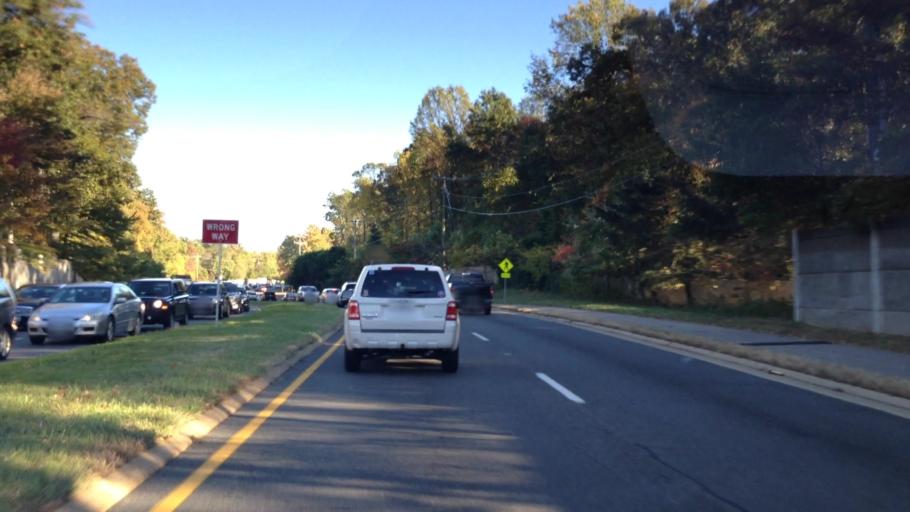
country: US
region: Virginia
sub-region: Fairfax County
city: Burke
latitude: 38.7502
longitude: -77.2635
